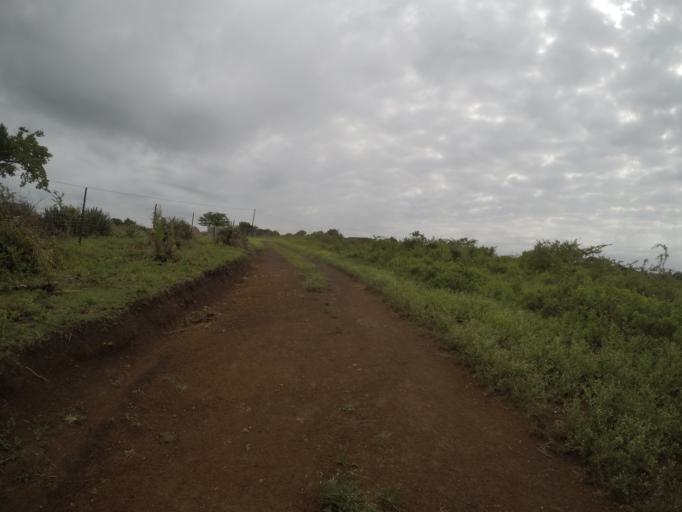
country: ZA
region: KwaZulu-Natal
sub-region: uThungulu District Municipality
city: Empangeni
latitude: -28.6421
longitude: 31.9030
